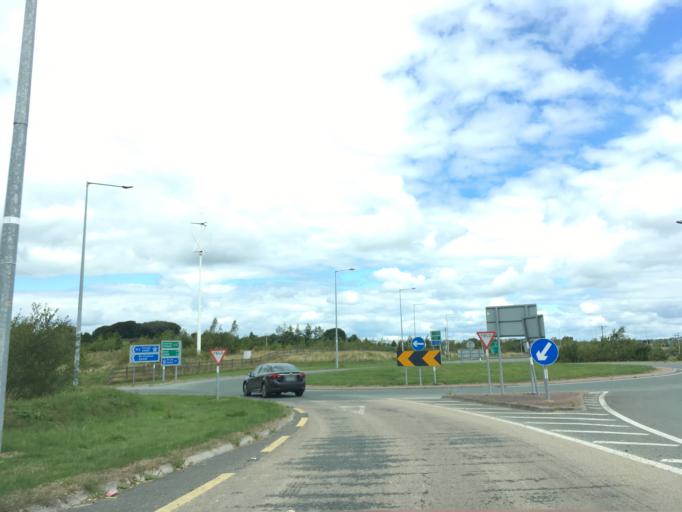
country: IE
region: Munster
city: Cashel
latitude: 52.4953
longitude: -7.8896
